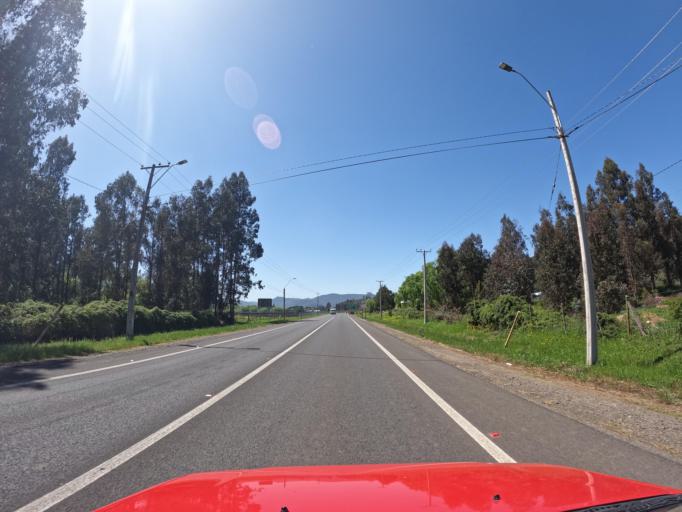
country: CL
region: Maule
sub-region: Provincia de Linares
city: Colbun
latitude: -35.7233
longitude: -71.4163
